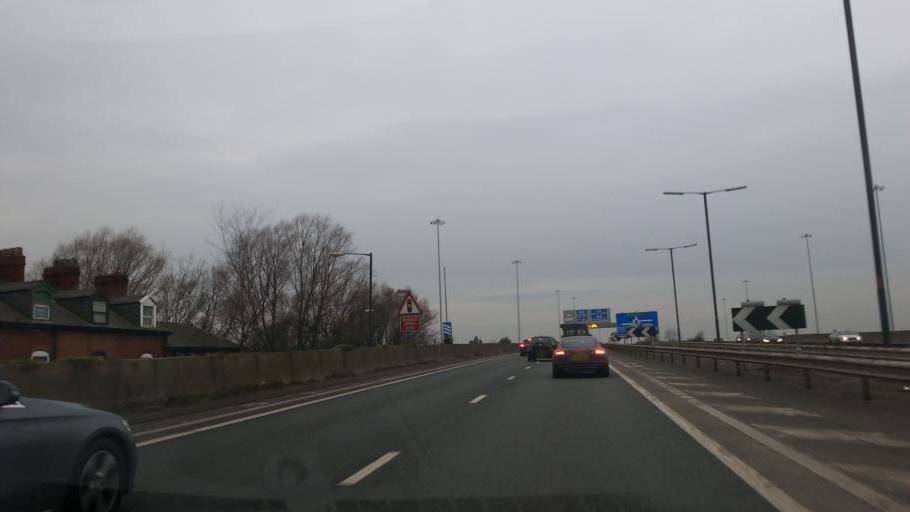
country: GB
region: England
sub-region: Borough of Tameside
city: Denton
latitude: 53.4564
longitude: -2.1277
